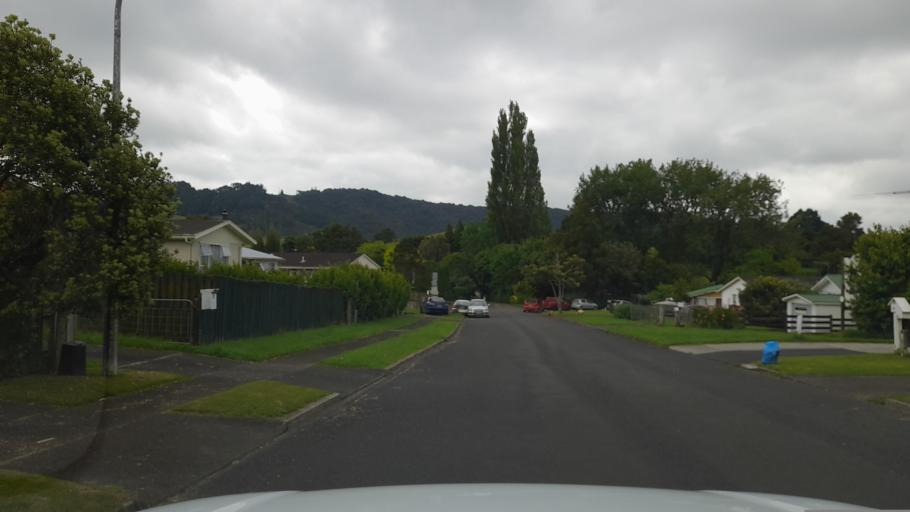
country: NZ
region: Northland
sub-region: Far North District
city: Waimate North
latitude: -35.4017
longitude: 173.7905
